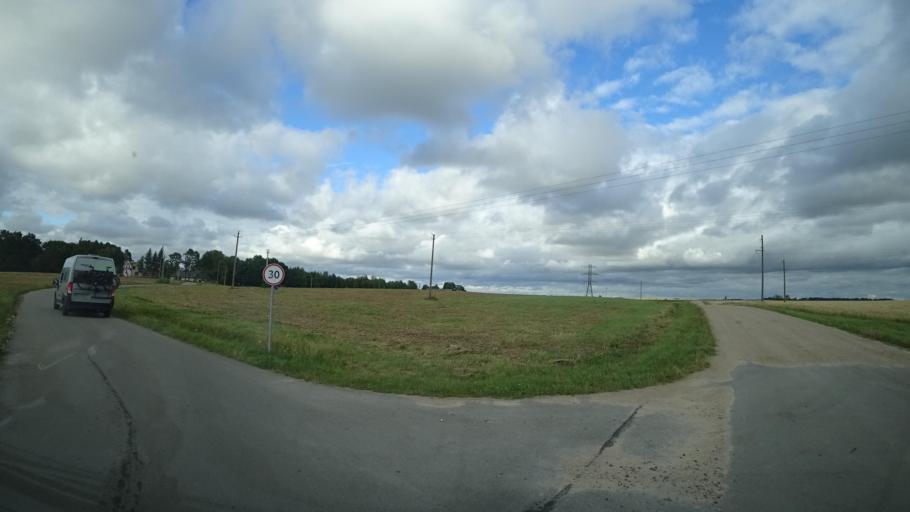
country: LT
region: Marijampoles apskritis
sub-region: Marijampole Municipality
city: Marijampole
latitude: 54.5173
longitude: 23.3270
